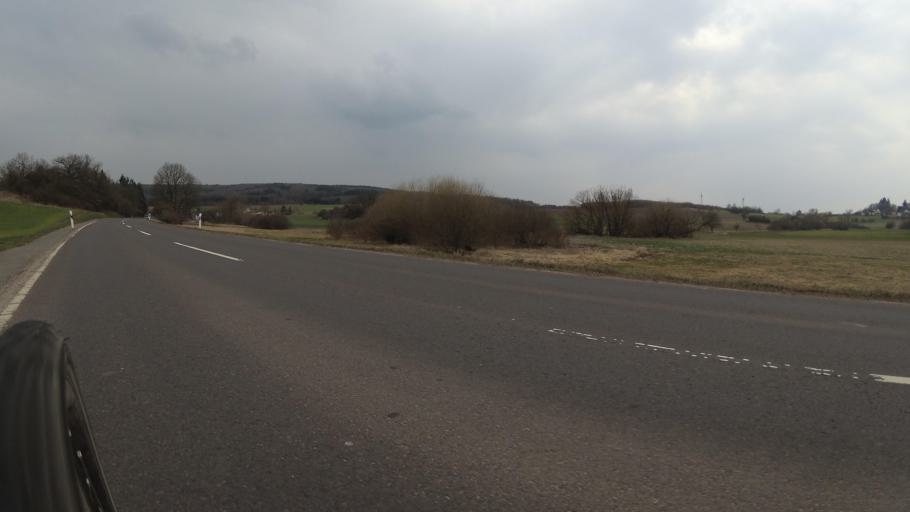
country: DE
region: Rheinland-Pfalz
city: Dienstweiler
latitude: 49.6410
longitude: 7.1778
